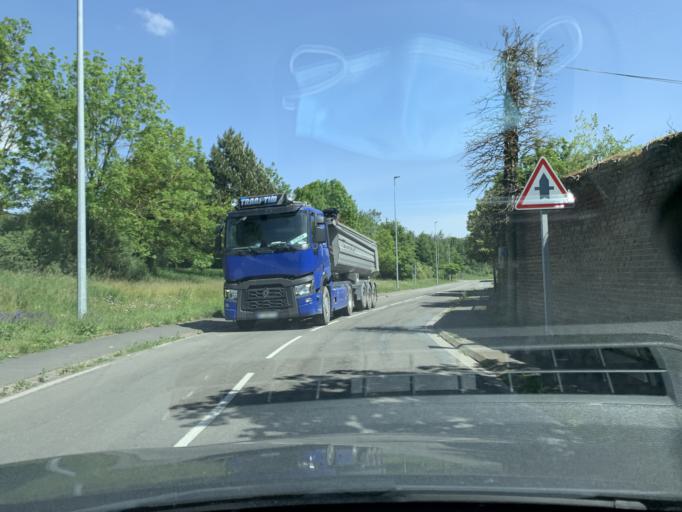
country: FR
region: Nord-Pas-de-Calais
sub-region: Departement du Nord
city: Masnieres
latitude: 50.1188
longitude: 3.1989
